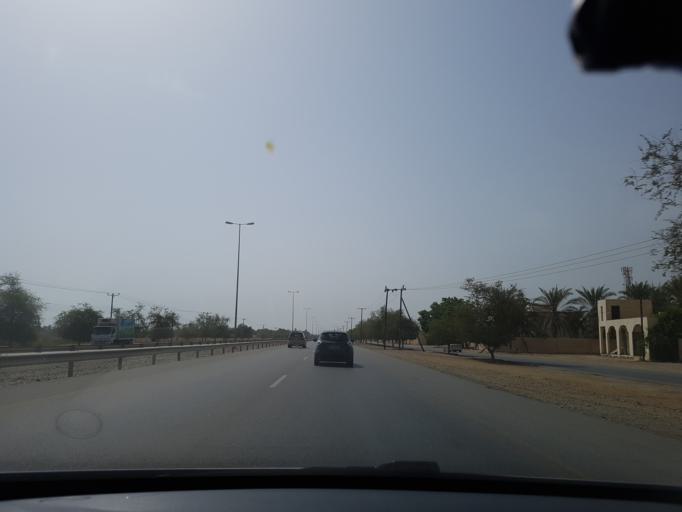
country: OM
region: Al Batinah
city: Al Khaburah
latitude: 23.9891
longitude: 57.0727
